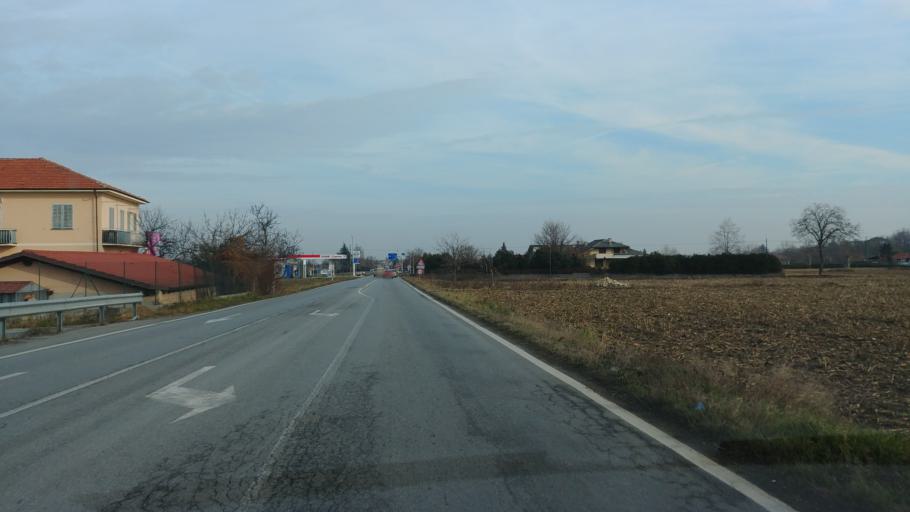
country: IT
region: Piedmont
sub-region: Provincia di Cuneo
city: Cuneo
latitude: 44.3789
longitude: 7.5576
